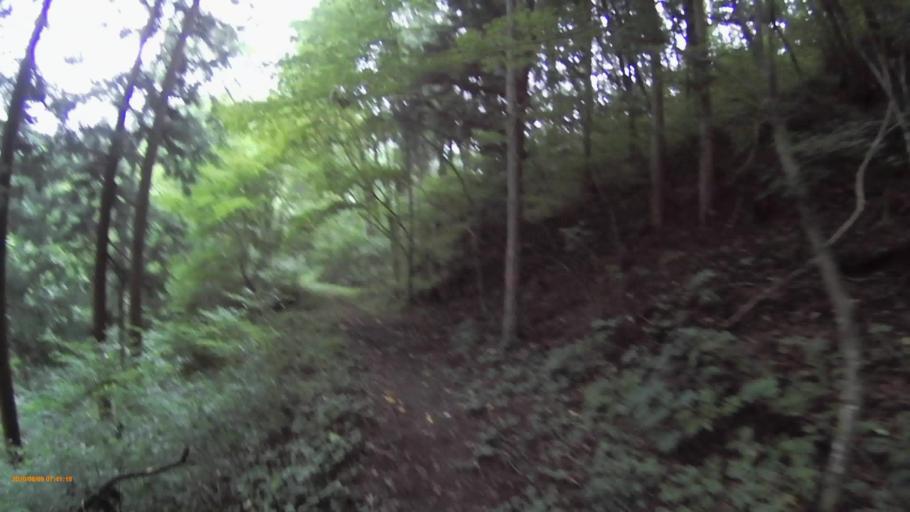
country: JP
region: Nagano
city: Tatsuno
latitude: 35.9579
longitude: 137.8041
